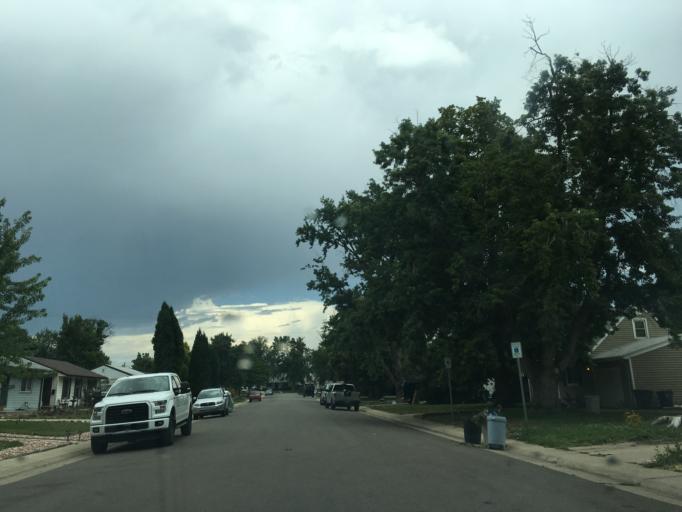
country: US
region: Colorado
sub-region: Arapahoe County
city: Sheridan
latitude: 39.6715
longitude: -105.0279
